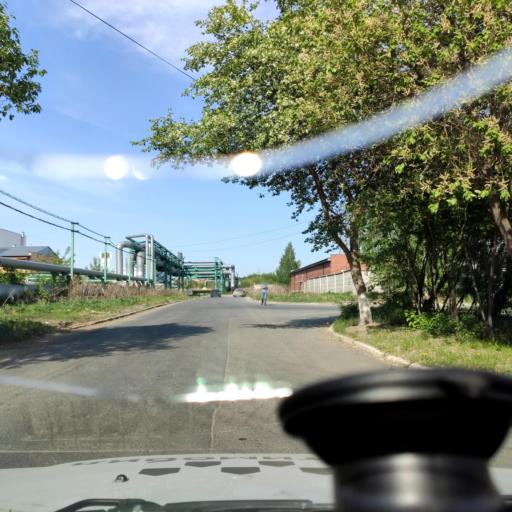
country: RU
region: Sverdlovsk
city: Sovkhoznyy
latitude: 56.7743
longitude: 60.5525
